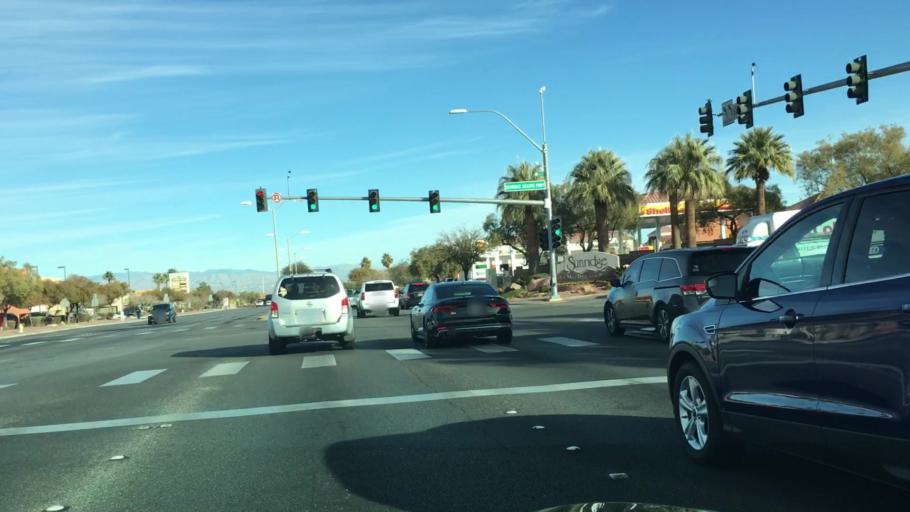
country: US
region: Nevada
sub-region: Clark County
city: Whitney
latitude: 35.9922
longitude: -115.1009
